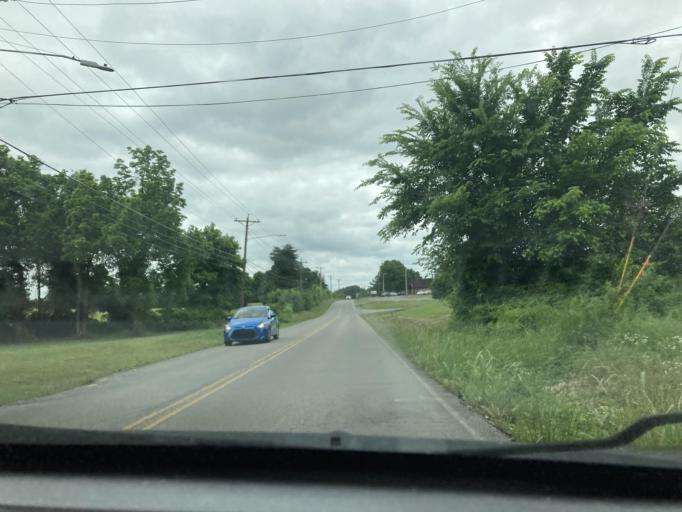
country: US
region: Tennessee
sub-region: Dickson County
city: Dickson
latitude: 36.0893
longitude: -87.3802
